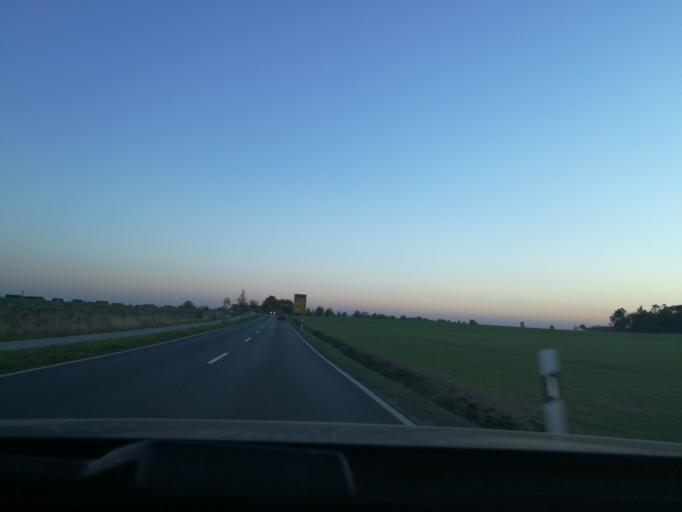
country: DE
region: Bavaria
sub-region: Regierungsbezirk Mittelfranken
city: Obermichelbach
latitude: 49.5205
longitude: 10.9018
